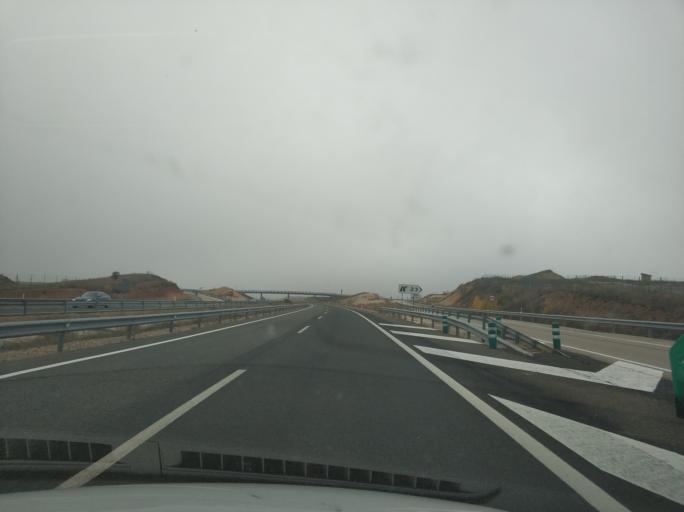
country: ES
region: Castille and Leon
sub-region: Provincia de Soria
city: Adradas
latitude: 41.3516
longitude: -2.4794
